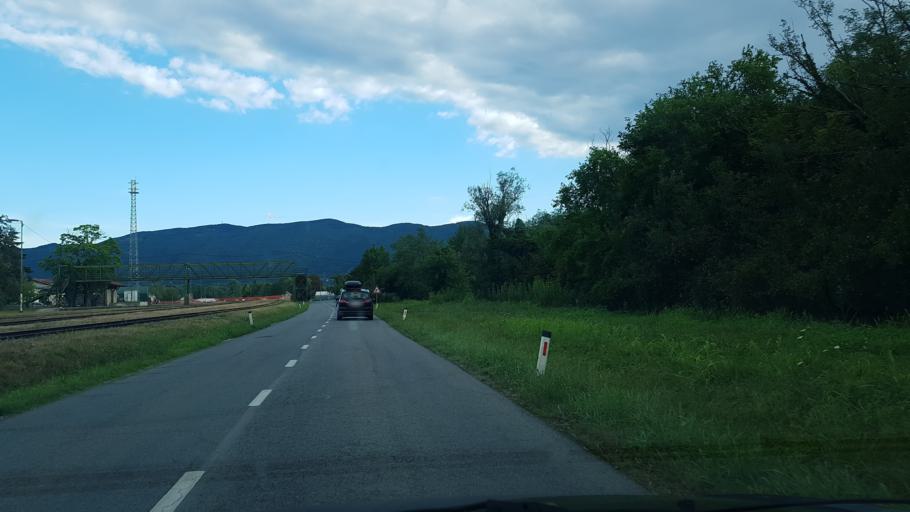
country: SI
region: Rence-Vogrsko
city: Volcja Draga
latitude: 45.9065
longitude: 13.6750
